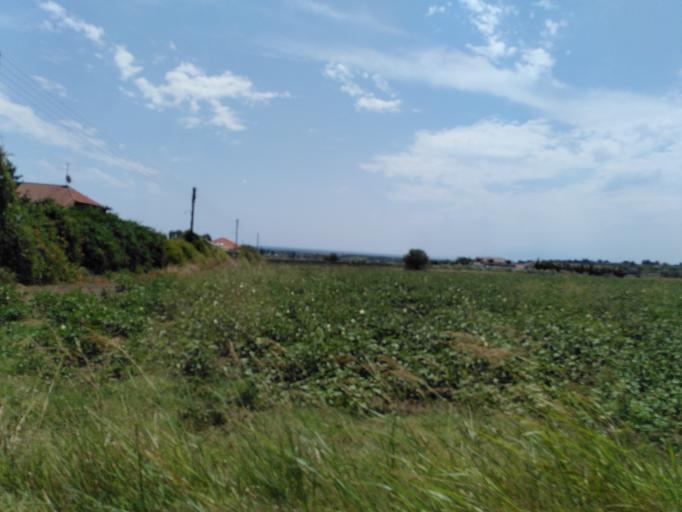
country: GR
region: Central Macedonia
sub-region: Nomos Thessalonikis
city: Epanomi
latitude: 40.4309
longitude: 22.9011
